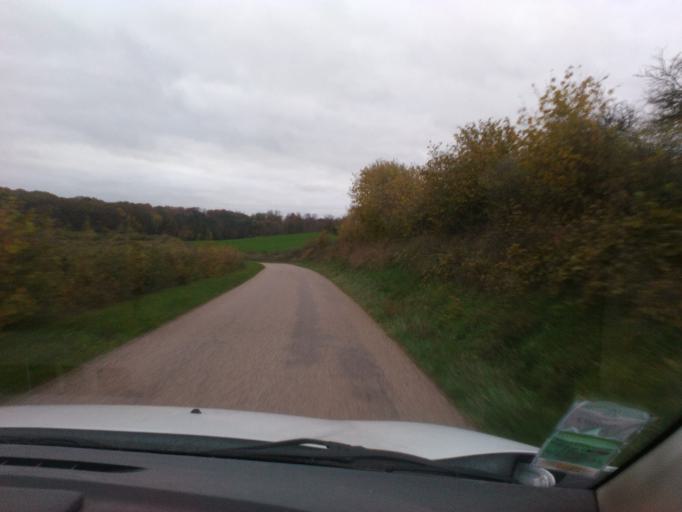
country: FR
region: Lorraine
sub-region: Departement des Vosges
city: Mirecourt
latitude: 48.3058
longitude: 6.2126
